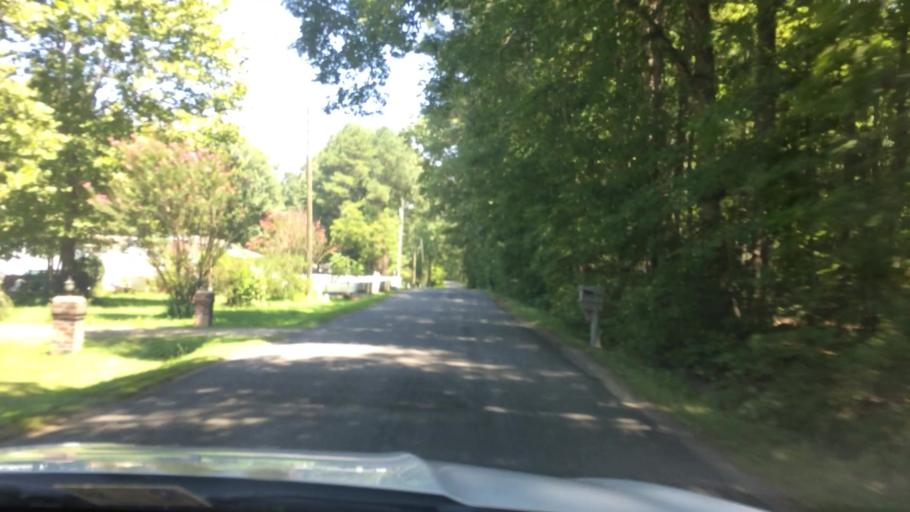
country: US
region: Virginia
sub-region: Charles City County
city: Charles City
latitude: 37.2686
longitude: -76.9420
